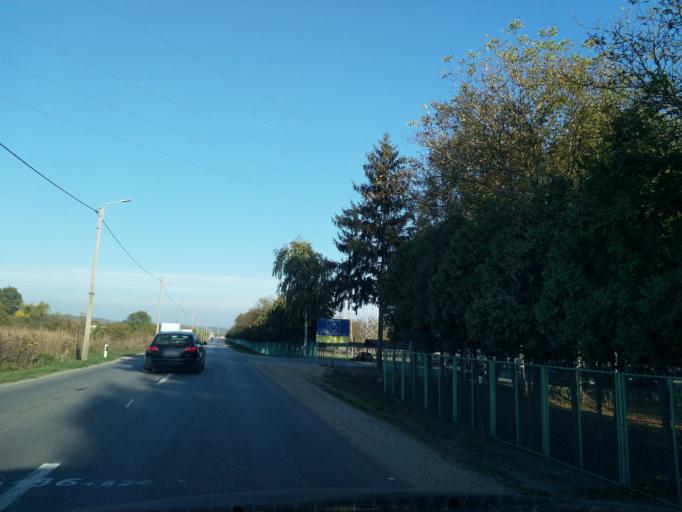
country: RS
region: Central Serbia
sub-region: Pomoravski Okrug
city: Svilajnac
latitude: 44.2260
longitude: 21.1604
